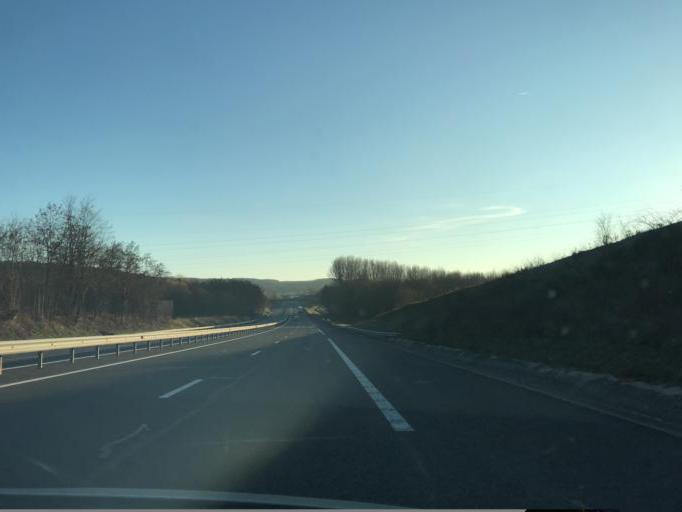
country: FR
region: Bourgogne
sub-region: Departement de l'Yonne
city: Saint-Martin-du-Tertre
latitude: 48.2274
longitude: 3.2416
